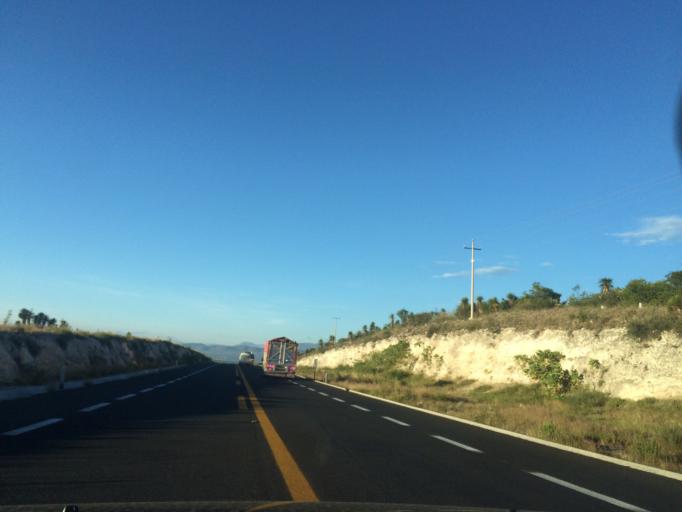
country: MX
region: Puebla
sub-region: Tehuacan
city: Magdalena Cuayucatepec
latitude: 18.5645
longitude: -97.4637
